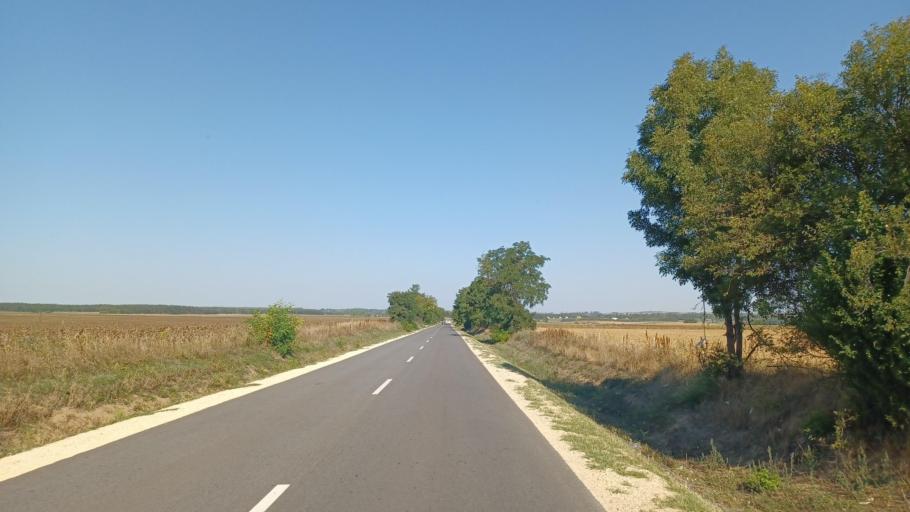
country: HU
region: Tolna
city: Paks
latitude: 46.6610
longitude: 18.8286
